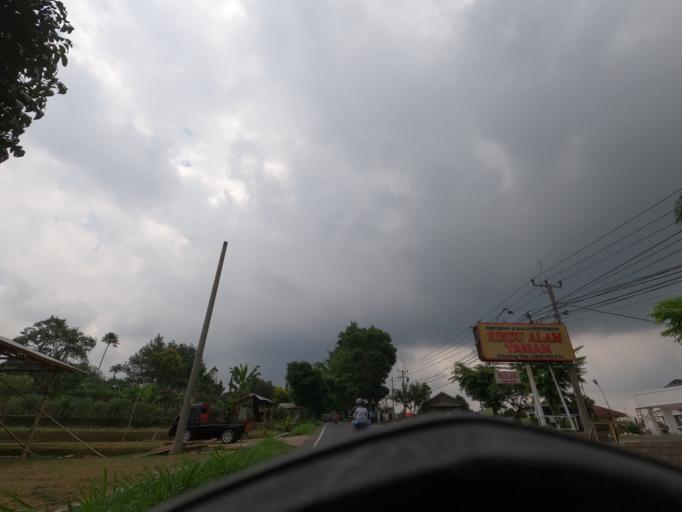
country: ID
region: West Java
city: Sukabumi
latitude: -6.7671
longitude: 107.0566
